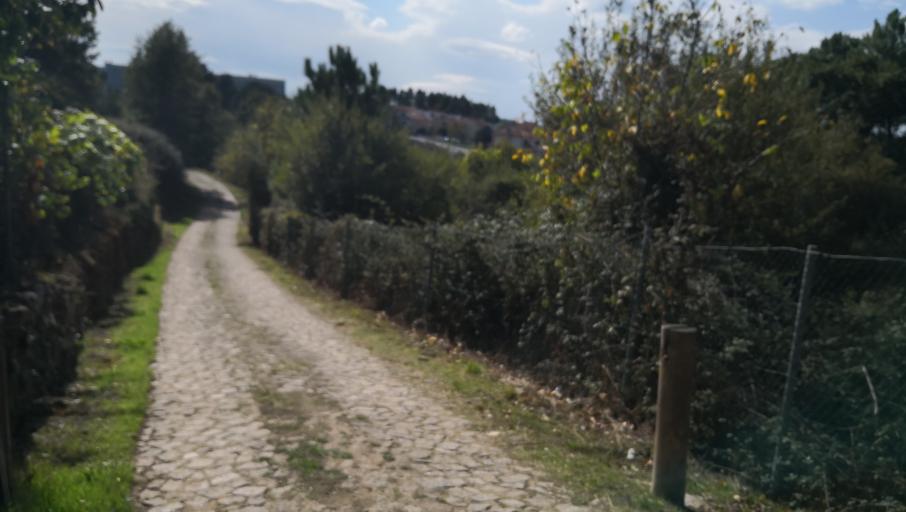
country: PT
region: Vila Real
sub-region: Vila Real
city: Vila Real
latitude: 41.3073
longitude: -7.7310
